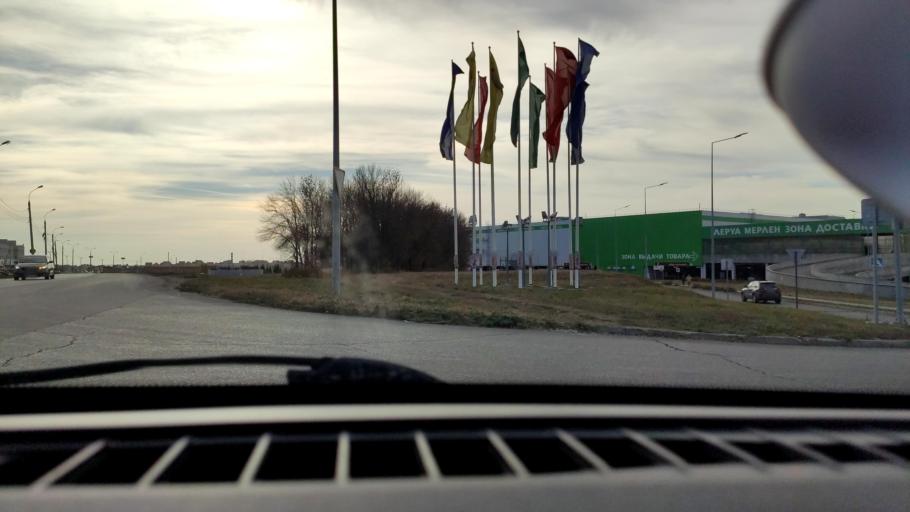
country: RU
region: Samara
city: Novosemeykino
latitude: 53.3279
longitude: 50.3113
